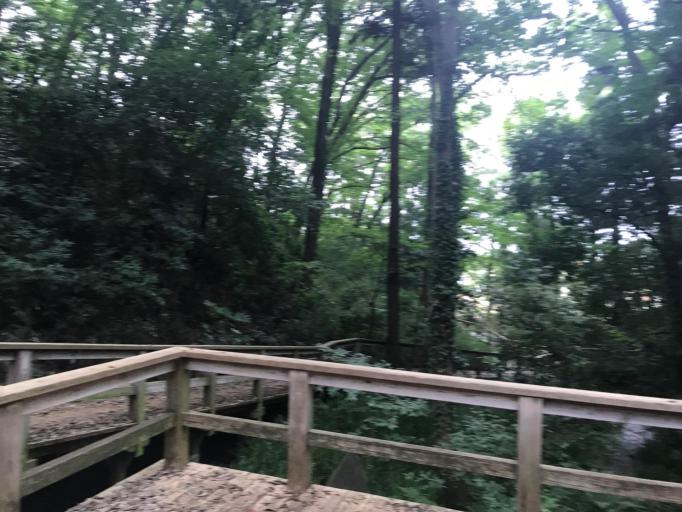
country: JP
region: Saitama
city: Asaka
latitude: 35.7768
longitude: 139.5766
